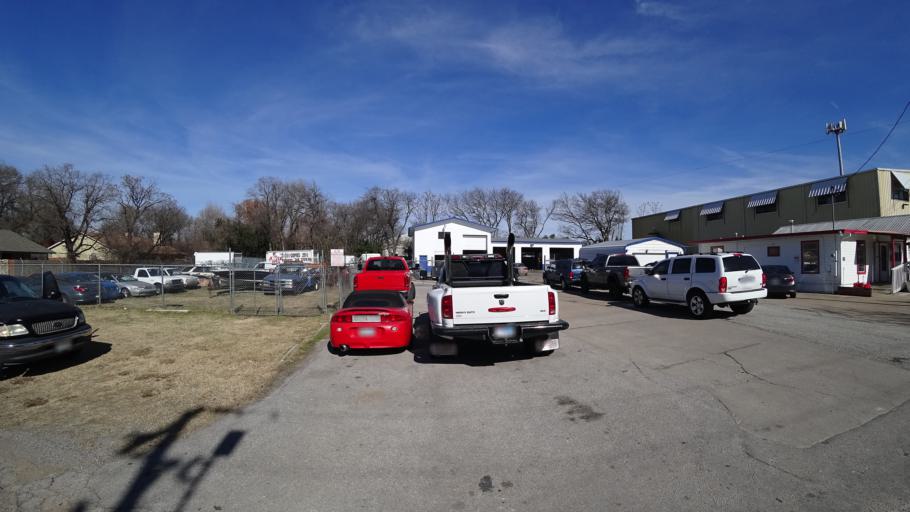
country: US
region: Texas
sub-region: Travis County
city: Wells Branch
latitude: 30.3709
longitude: -97.6945
